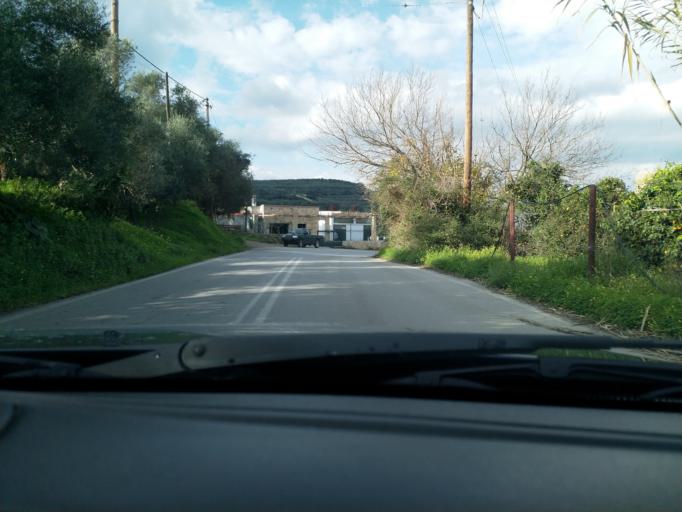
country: GR
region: Crete
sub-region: Nomos Chanias
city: Gerani
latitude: 35.5021
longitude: 23.8969
